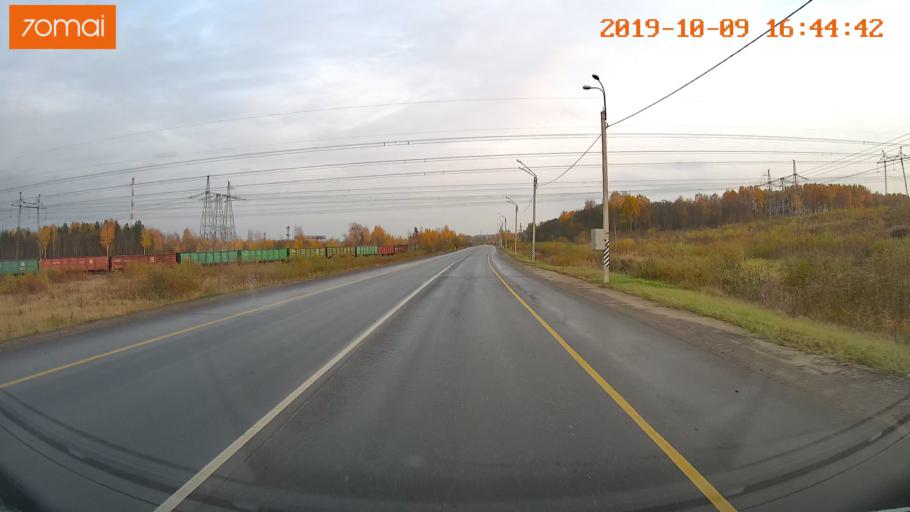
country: RU
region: Kostroma
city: Volgorechensk
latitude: 57.4505
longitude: 41.1447
